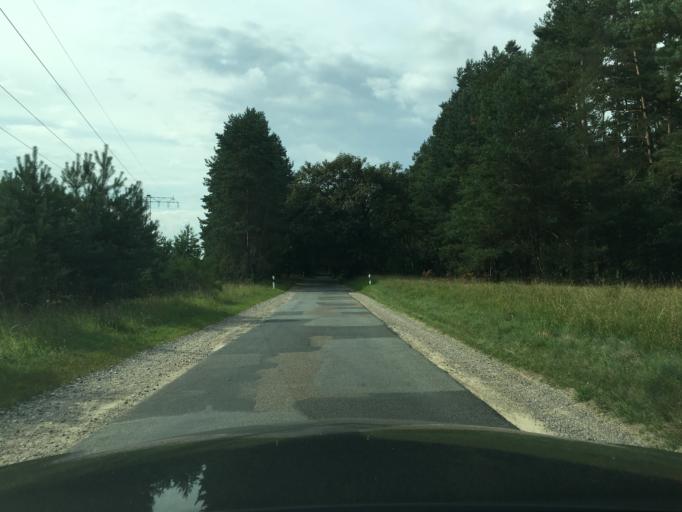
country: DE
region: Mecklenburg-Vorpommern
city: Waren
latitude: 53.4719
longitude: 12.7837
